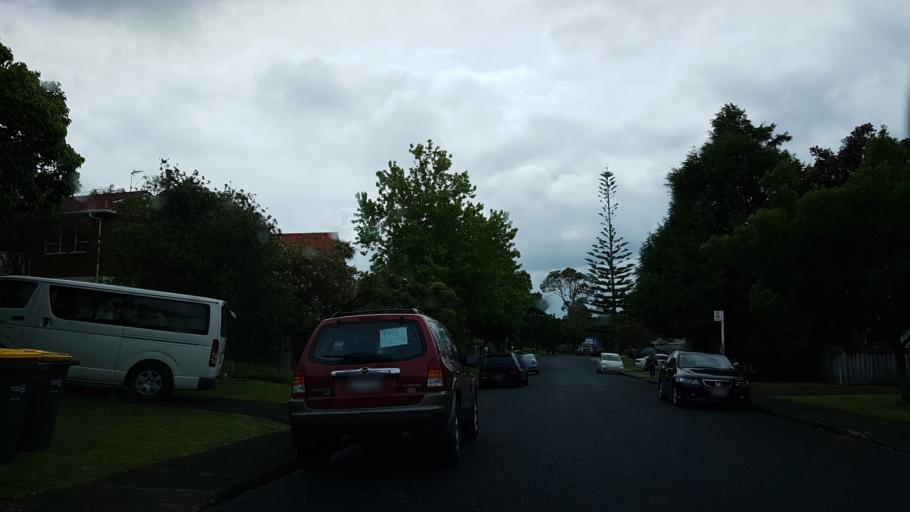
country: NZ
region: Auckland
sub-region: Auckland
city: North Shore
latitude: -36.7911
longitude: 174.7328
